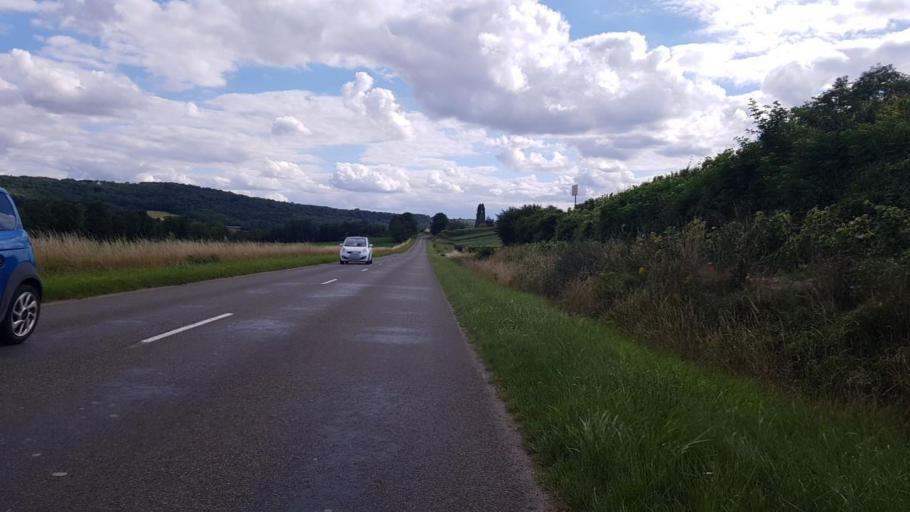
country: FR
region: Picardie
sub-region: Departement de l'Aisne
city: Crezancy
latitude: 49.0580
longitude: 3.4746
